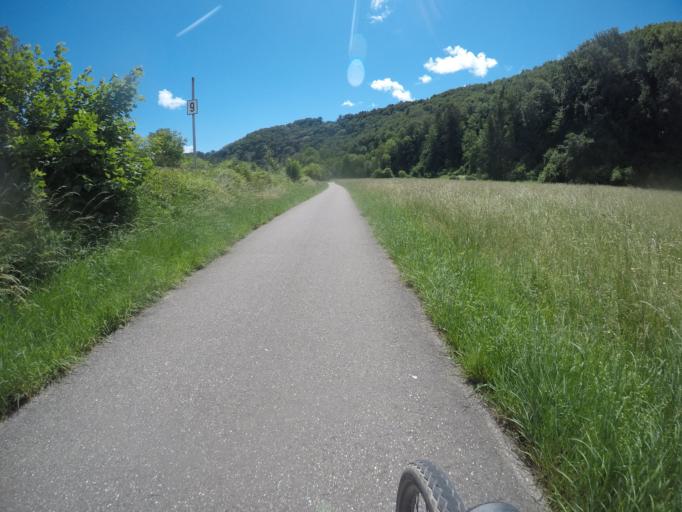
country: DE
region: Baden-Wuerttemberg
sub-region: Karlsruhe Region
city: Horb am Neckar
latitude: 48.4452
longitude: 8.7063
